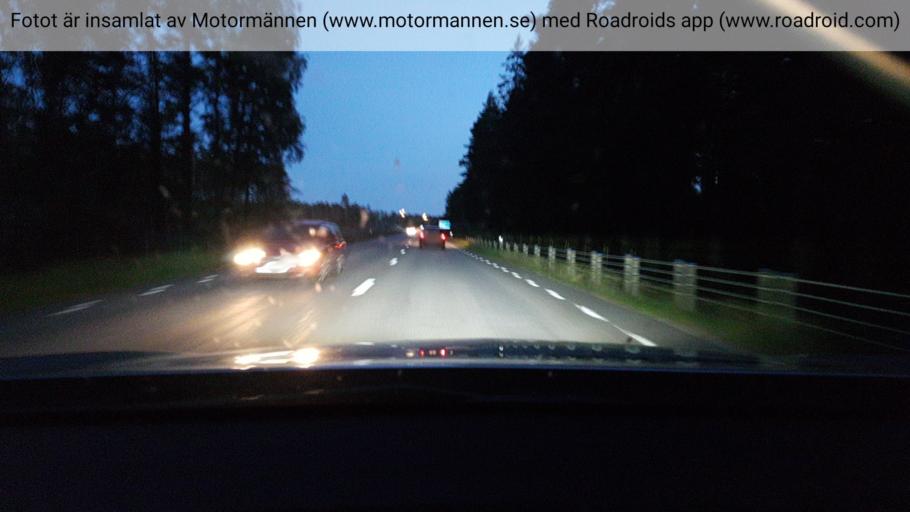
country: SE
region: Vaestra Goetaland
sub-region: Tibro Kommun
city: Tibro
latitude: 58.4482
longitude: 14.1927
